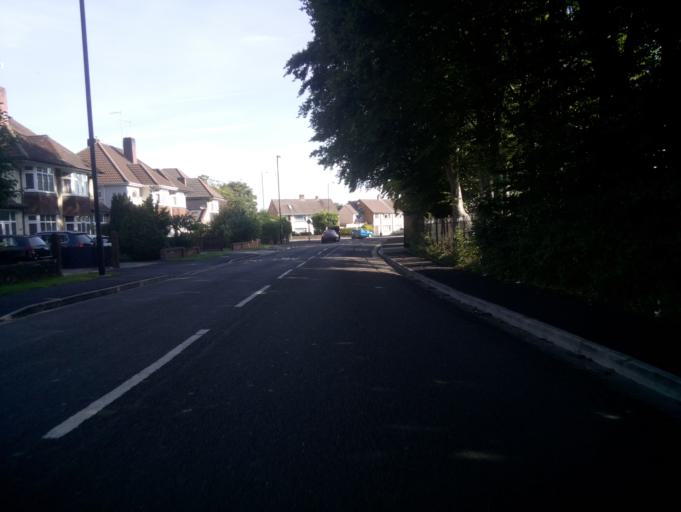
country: GB
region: England
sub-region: Bath and North East Somerset
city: Whitchurch
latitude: 51.4256
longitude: -2.5571
